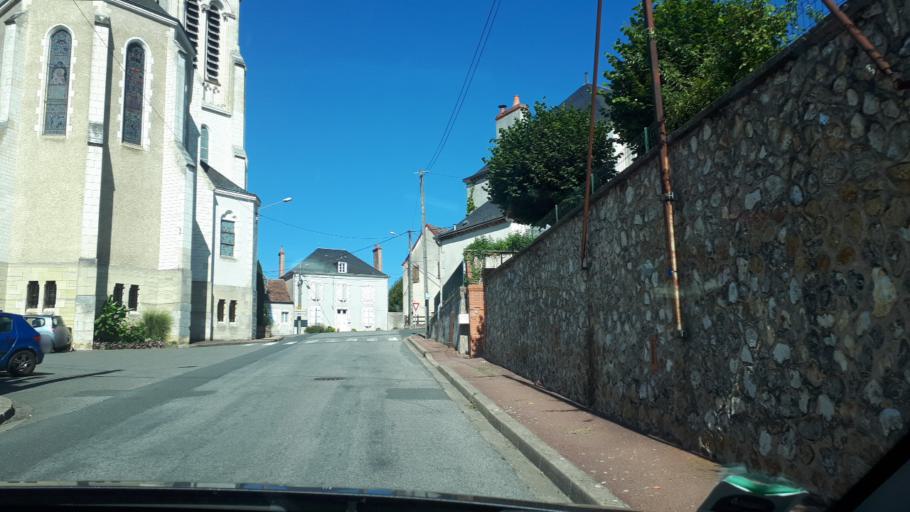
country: FR
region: Centre
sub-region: Departement du Loiret
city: Autry-le-Chatel
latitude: 47.5977
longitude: 2.6024
